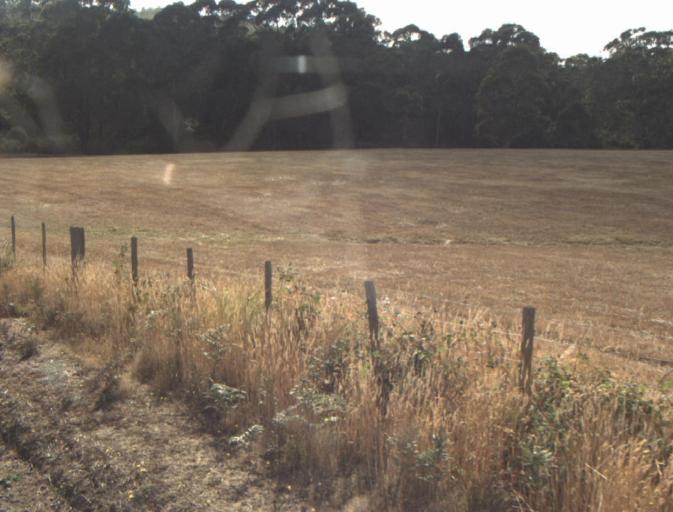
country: AU
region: Tasmania
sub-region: Dorset
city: Bridport
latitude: -41.1513
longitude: 147.2306
